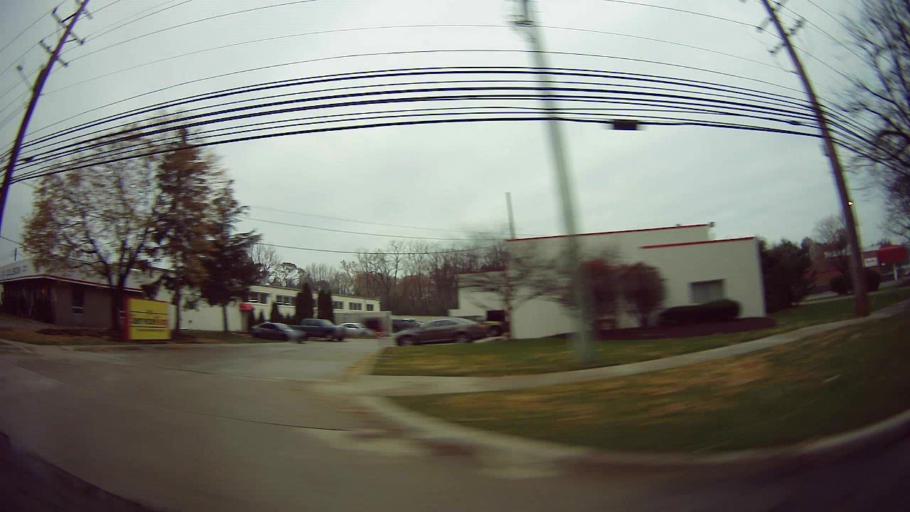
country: US
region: Michigan
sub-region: Oakland County
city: Bingham Farms
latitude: 42.4683
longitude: -83.2799
